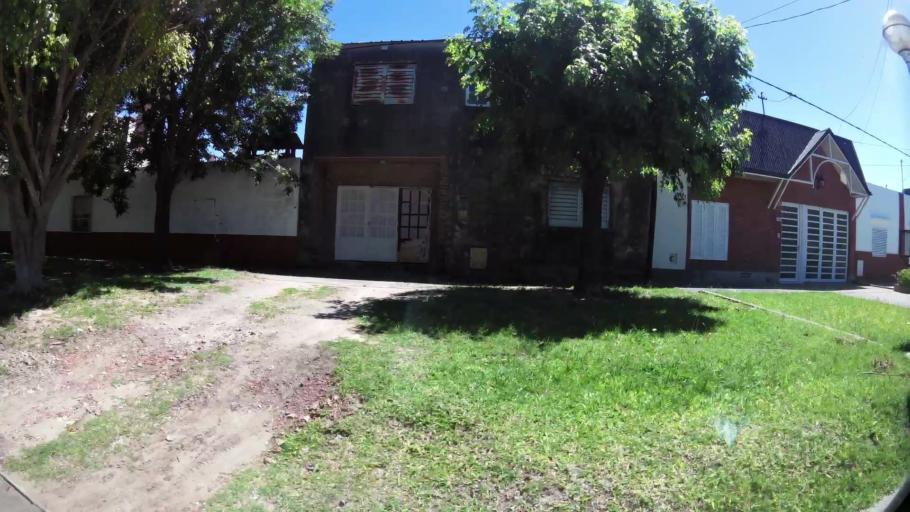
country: AR
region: Santa Fe
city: Santa Fe de la Vera Cruz
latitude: -31.6284
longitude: -60.7162
